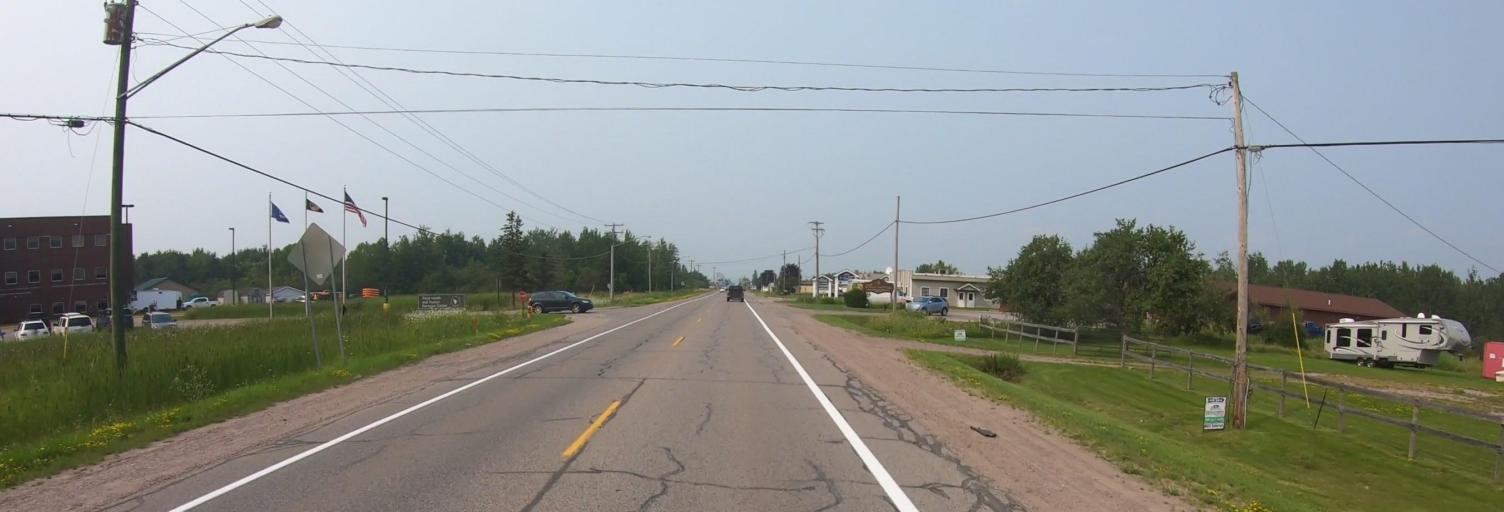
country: US
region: Michigan
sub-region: Chippewa County
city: Sault Ste. Marie
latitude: 46.4667
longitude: -84.3540
